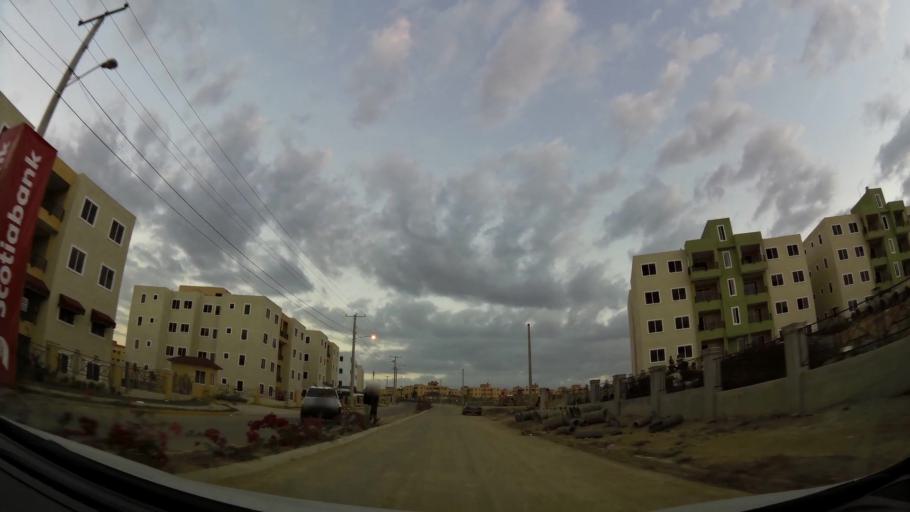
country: DO
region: Nacional
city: La Agustina
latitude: 18.5651
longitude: -69.9461
